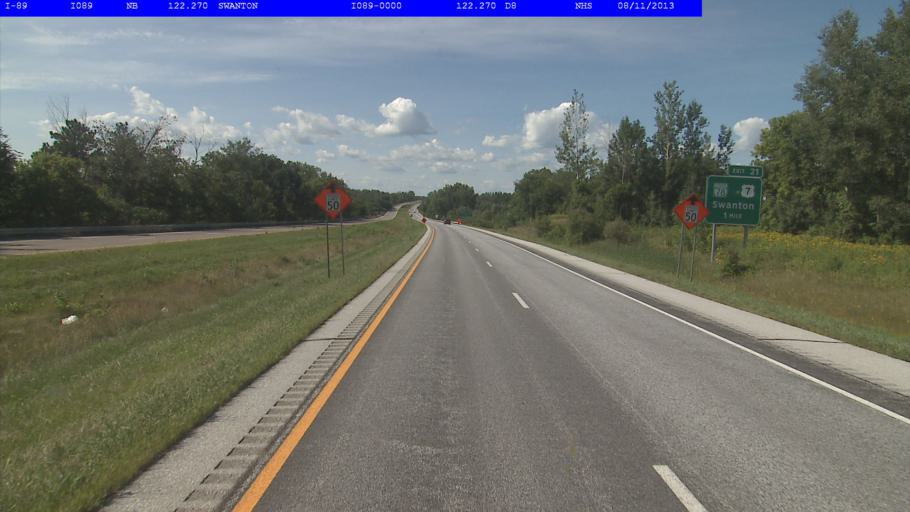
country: US
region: Vermont
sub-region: Franklin County
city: Swanton
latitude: 44.9076
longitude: -73.0987
